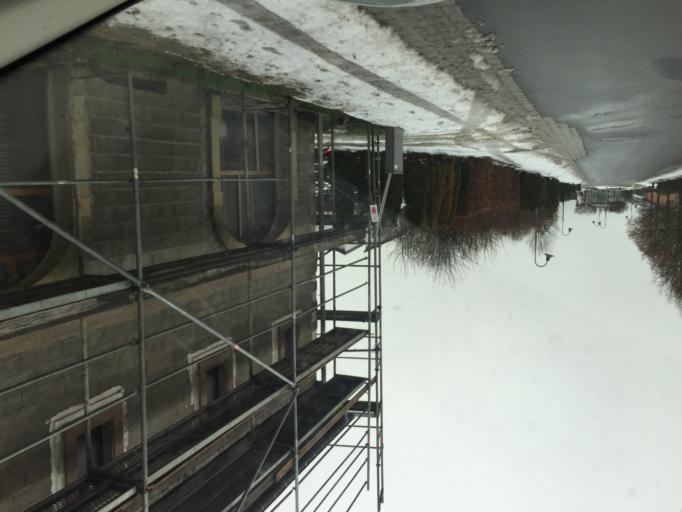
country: LU
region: Diekirch
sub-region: Canton de Diekirch
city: Niederfeulen
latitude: 49.8467
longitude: 6.0314
